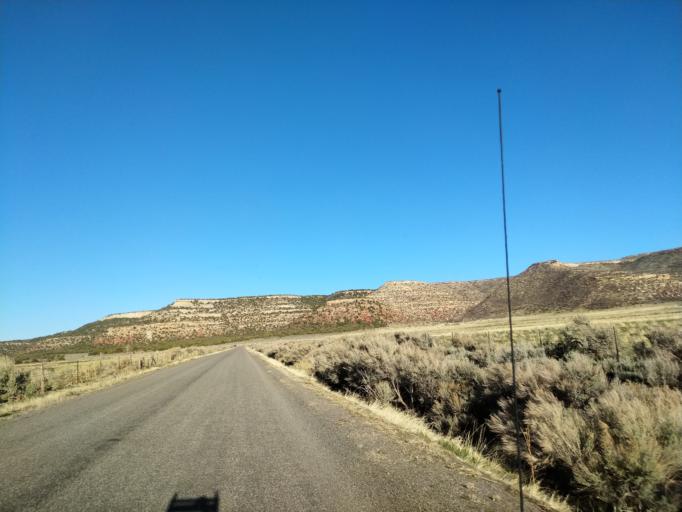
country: US
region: Colorado
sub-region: Mesa County
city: Loma
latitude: 38.9490
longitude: -109.0366
